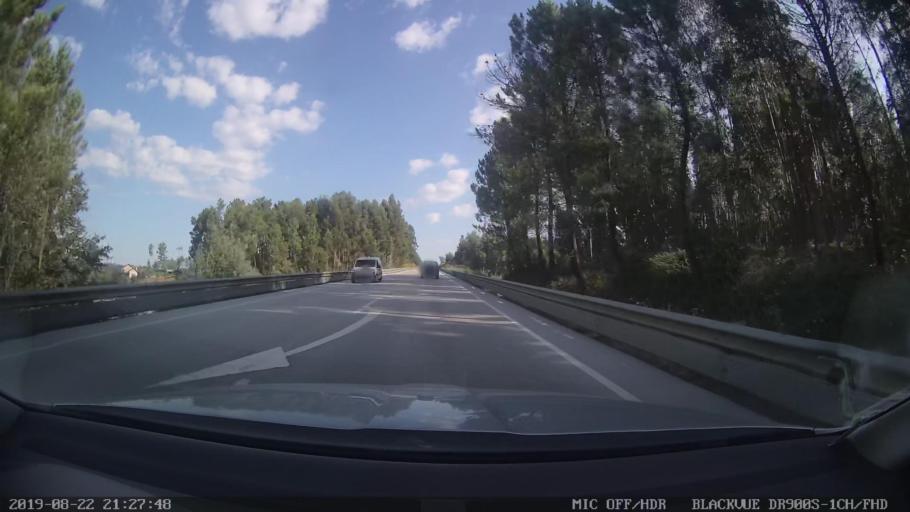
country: PT
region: Leiria
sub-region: Pedrogao Grande
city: Pedrogao Grande
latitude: 39.8838
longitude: -8.1201
